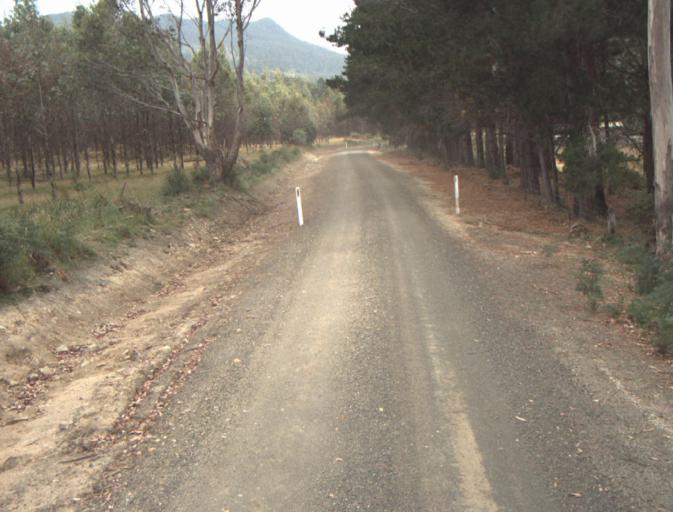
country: AU
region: Tasmania
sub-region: Northern Midlands
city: Evandale
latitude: -41.4559
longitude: 147.4450
